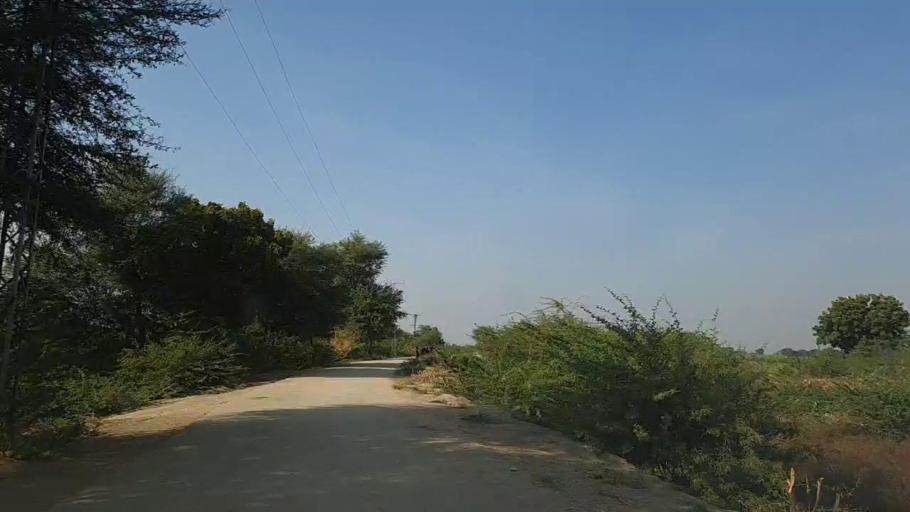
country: PK
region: Sindh
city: Naukot
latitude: 24.9361
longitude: 69.4591
